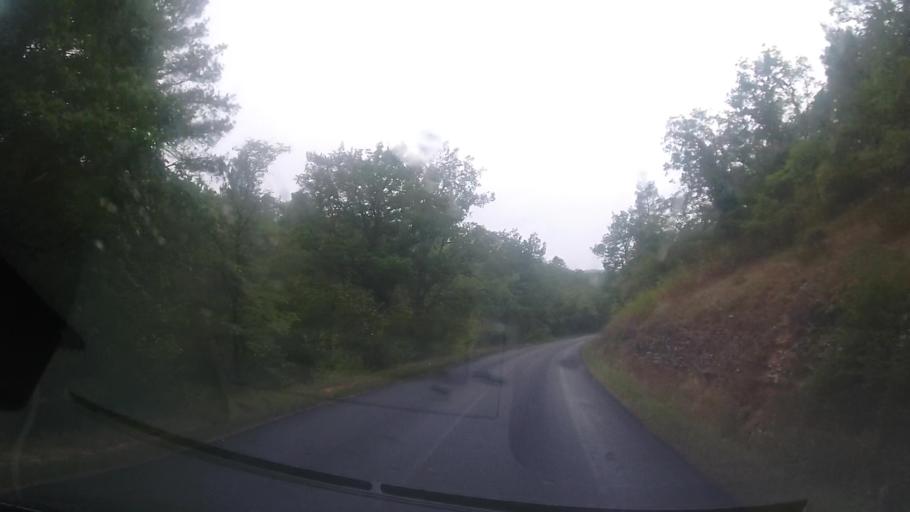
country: FR
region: Aquitaine
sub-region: Departement de la Dordogne
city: Cenac-et-Saint-Julien
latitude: 44.7894
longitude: 1.1825
